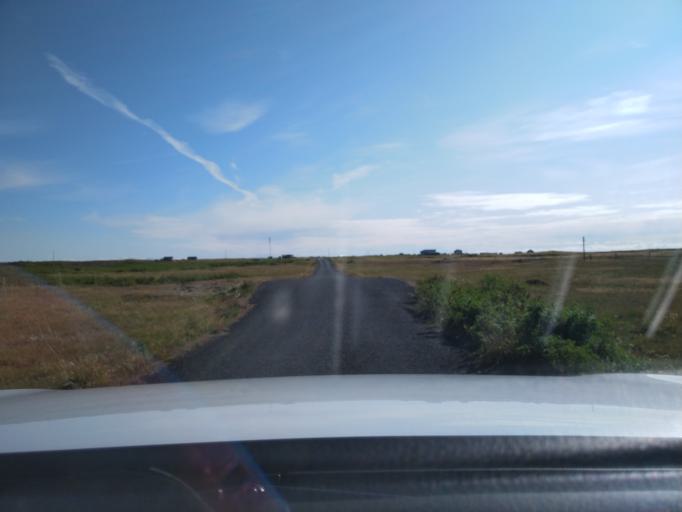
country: IS
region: South
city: THorlakshoefn
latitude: 63.8335
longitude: -21.6974
